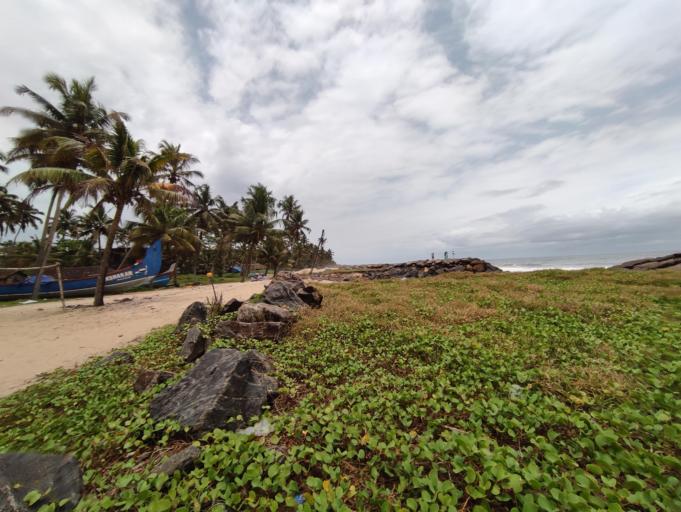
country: IN
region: Kerala
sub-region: Alappuzha
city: Vayalar
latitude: 9.6867
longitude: 76.2900
